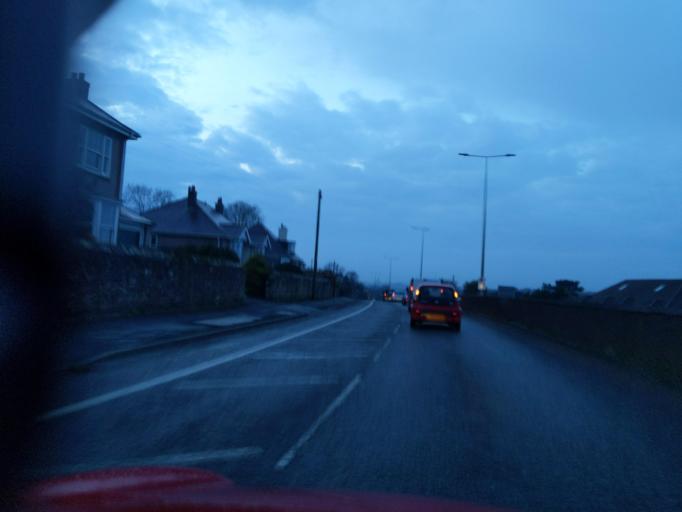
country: GB
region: England
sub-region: Plymouth
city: Plymstock
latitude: 50.3622
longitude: -4.0679
